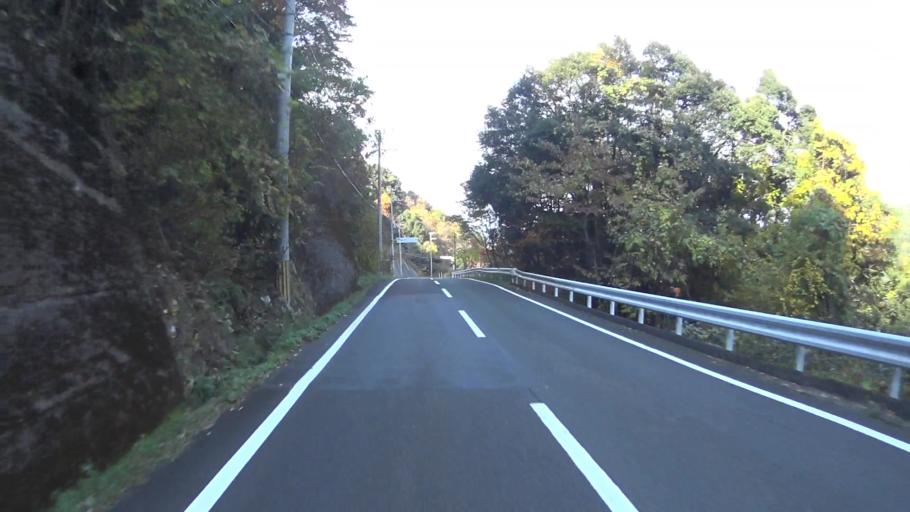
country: JP
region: Kyoto
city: Maizuru
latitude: 35.5430
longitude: 135.3963
